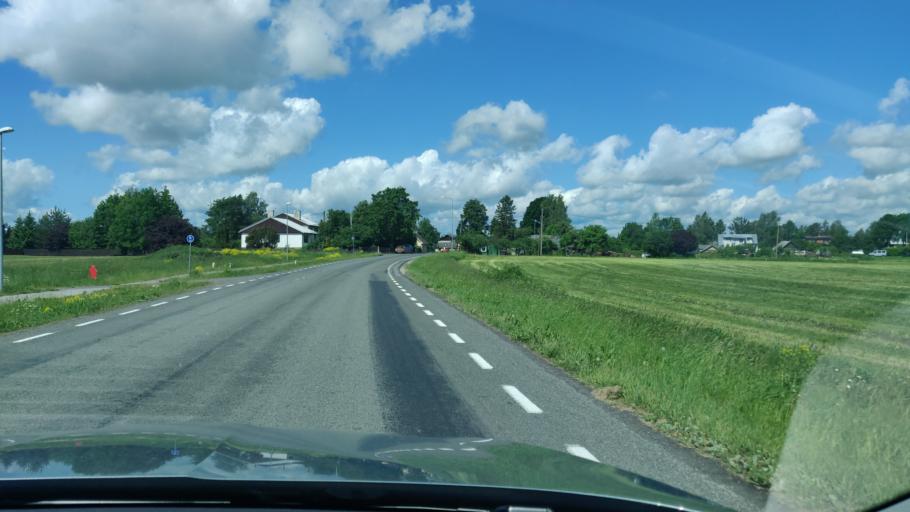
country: EE
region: Jaervamaa
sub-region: Paide linn
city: Paide
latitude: 58.8798
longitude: 25.5895
